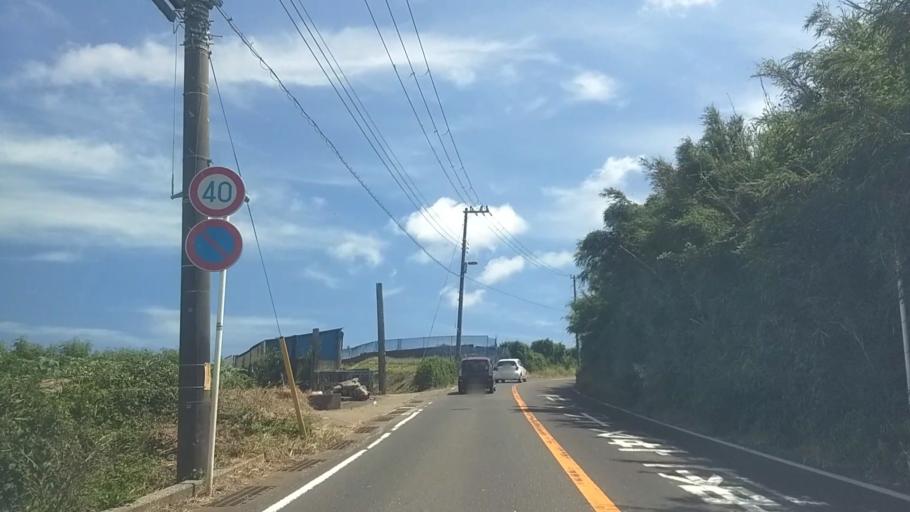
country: JP
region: Kanagawa
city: Miura
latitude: 35.2002
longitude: 139.6509
